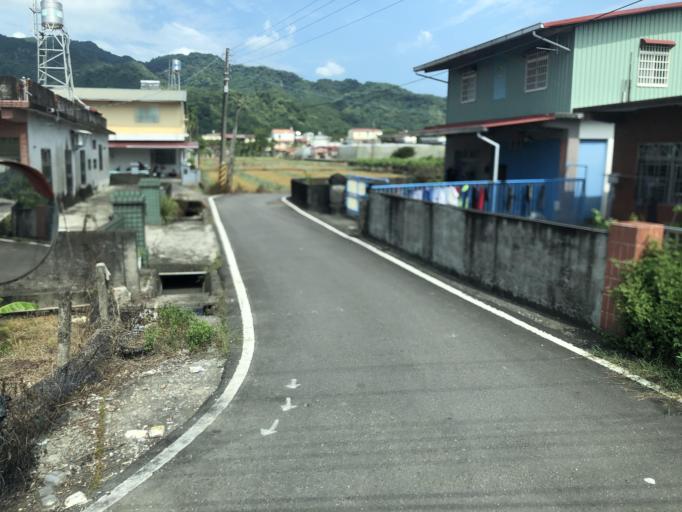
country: TW
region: Taiwan
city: Yujing
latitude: 22.9144
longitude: 120.5668
